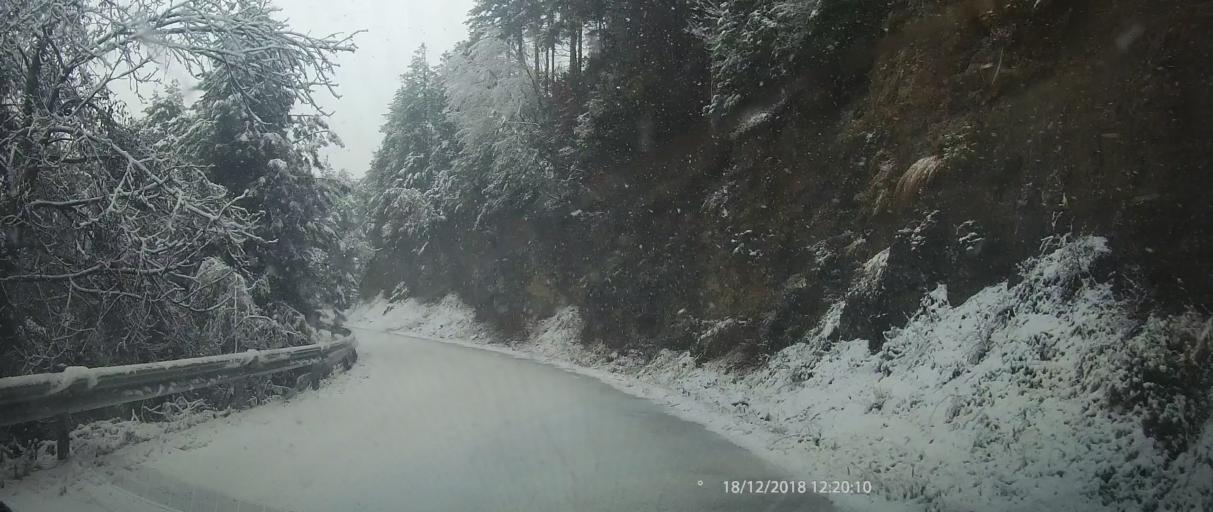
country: GR
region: Central Macedonia
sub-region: Nomos Pierias
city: Litochoro
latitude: 40.0972
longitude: 22.4231
